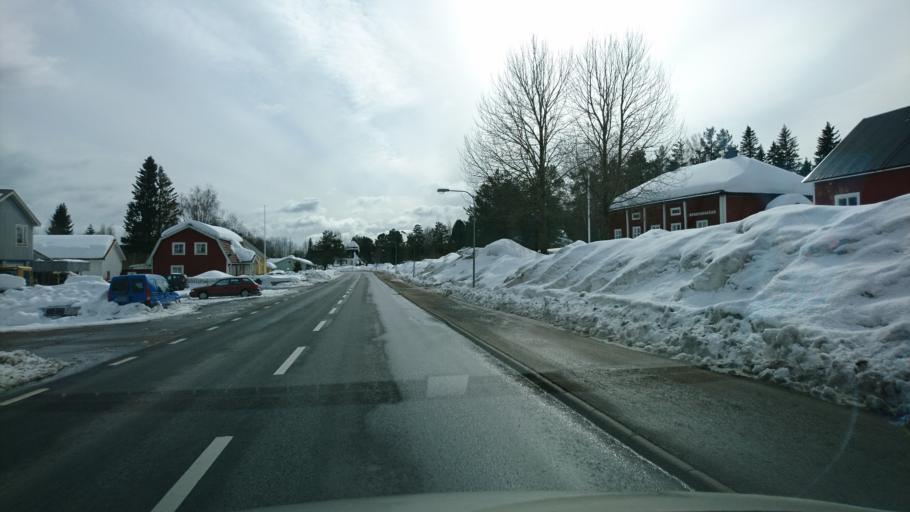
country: SE
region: Vaesternorrland
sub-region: Timra Kommun
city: Bergeforsen
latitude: 62.7718
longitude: 17.4201
